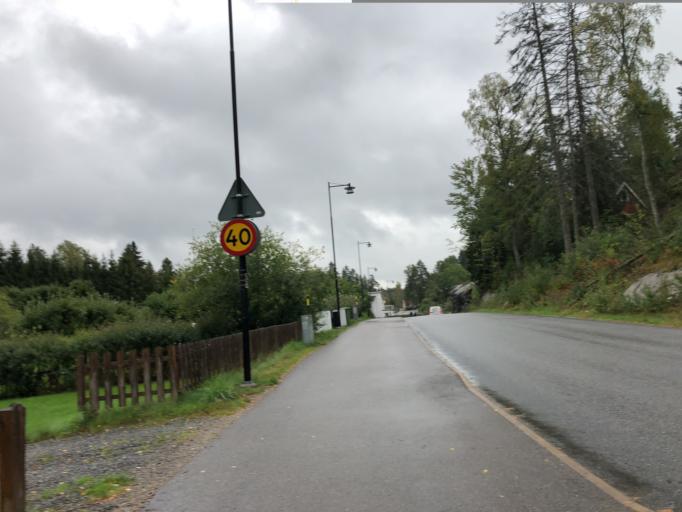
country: SE
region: Stockholm
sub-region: Tyreso Kommun
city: Bollmora
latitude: 59.2084
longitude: 18.2133
